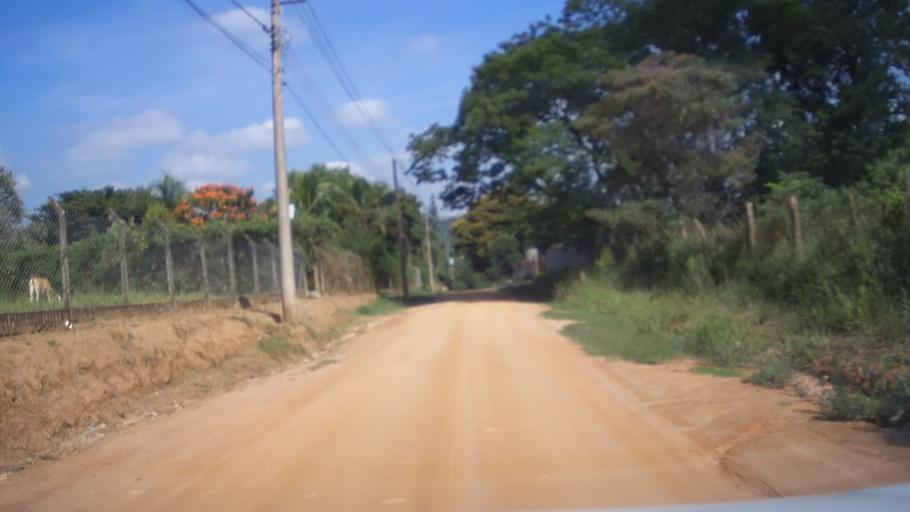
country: BR
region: Sao Paulo
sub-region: Itupeva
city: Itupeva
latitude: -23.2188
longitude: -47.0710
